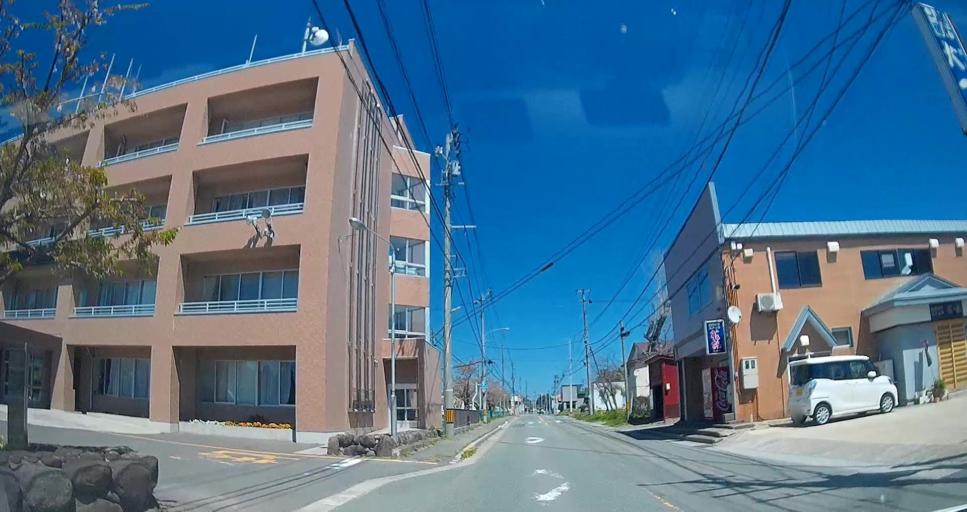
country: JP
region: Aomori
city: Misawa
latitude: 40.9671
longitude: 141.3749
